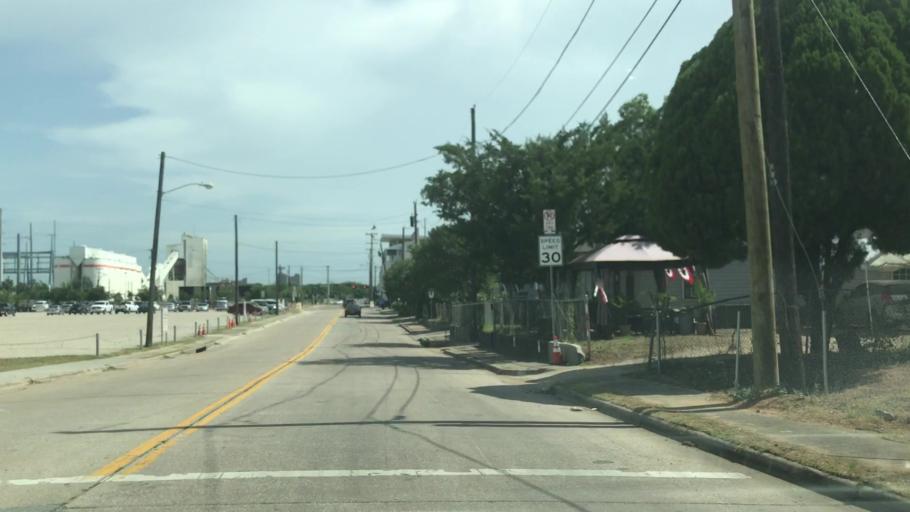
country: US
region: Texas
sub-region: Dallas County
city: Dallas
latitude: 32.7810
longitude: -96.8277
